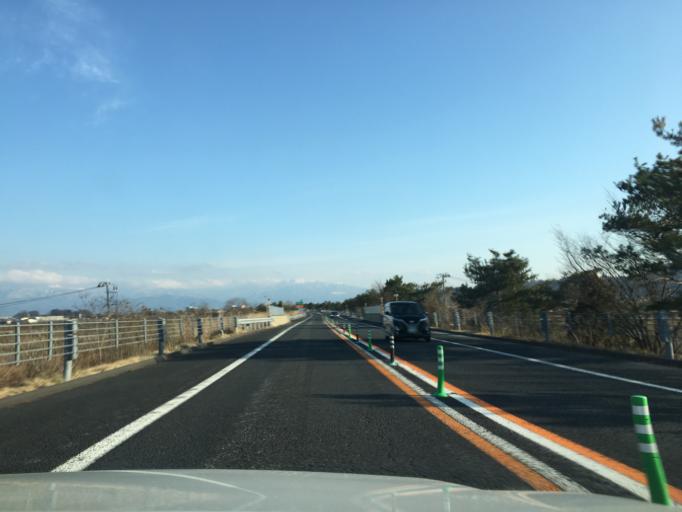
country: JP
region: Yamagata
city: Sagae
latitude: 38.3755
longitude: 140.2441
